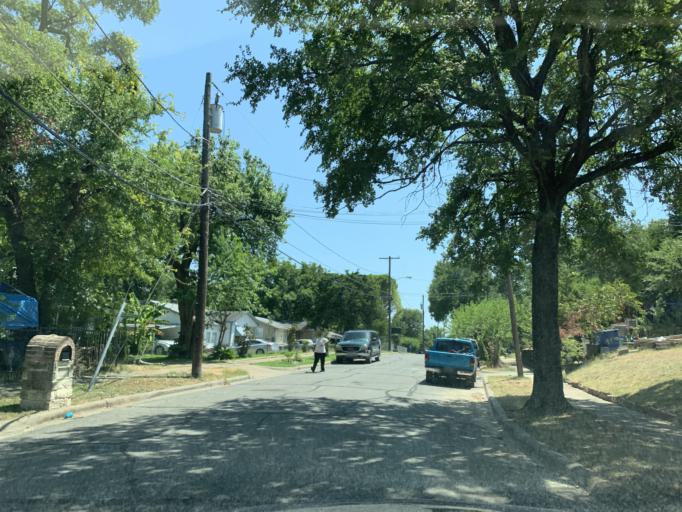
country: US
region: Texas
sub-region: Dallas County
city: Cockrell Hill
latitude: 32.6906
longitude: -96.8099
